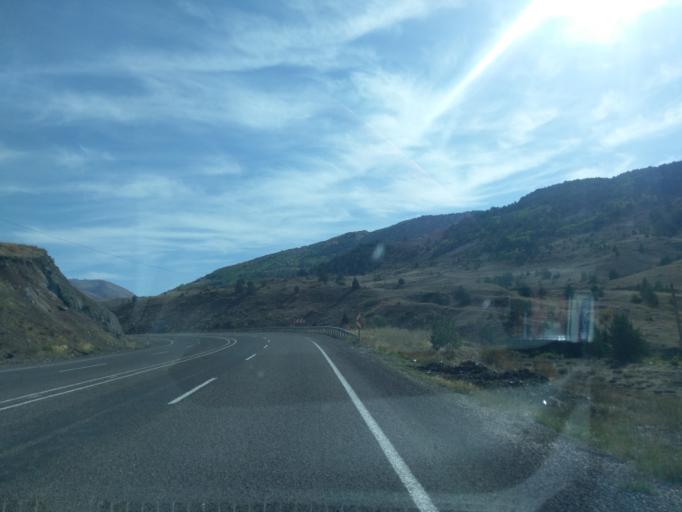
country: TR
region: Sivas
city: Imranli
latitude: 39.8552
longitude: 38.3053
